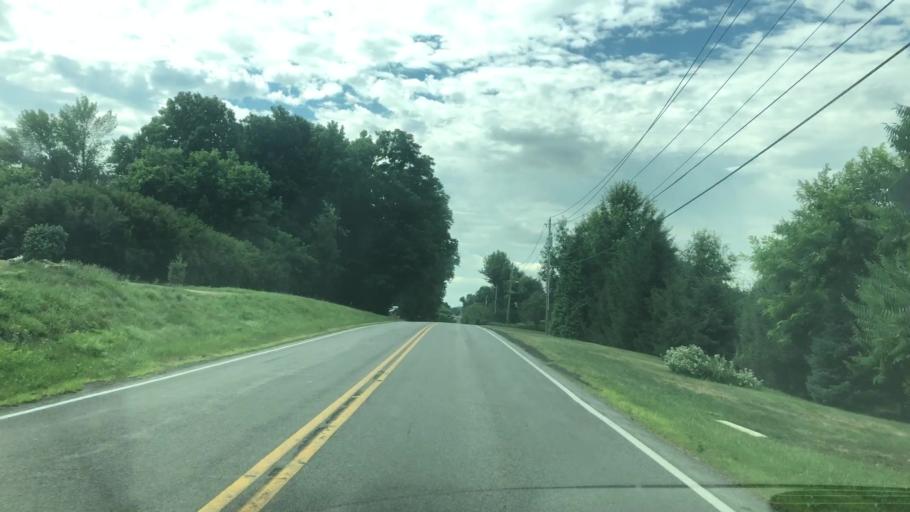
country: US
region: New York
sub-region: Monroe County
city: Fairport
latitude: 43.0777
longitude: -77.3922
